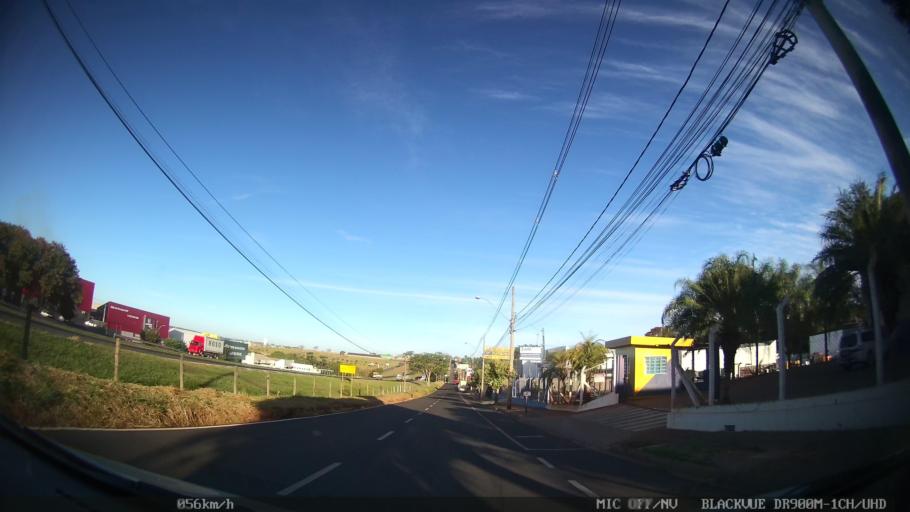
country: BR
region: Sao Paulo
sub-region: Sao Jose Do Rio Preto
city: Sao Jose do Rio Preto
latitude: -20.8578
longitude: -49.3380
